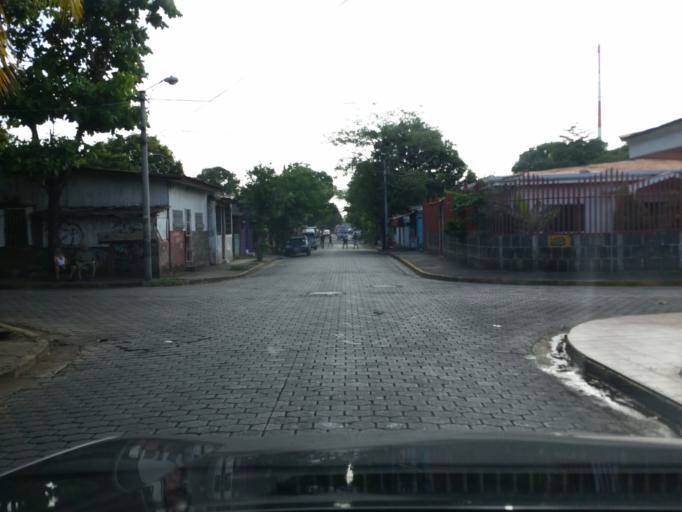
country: NI
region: Managua
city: Managua
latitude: 12.1405
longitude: -86.2494
